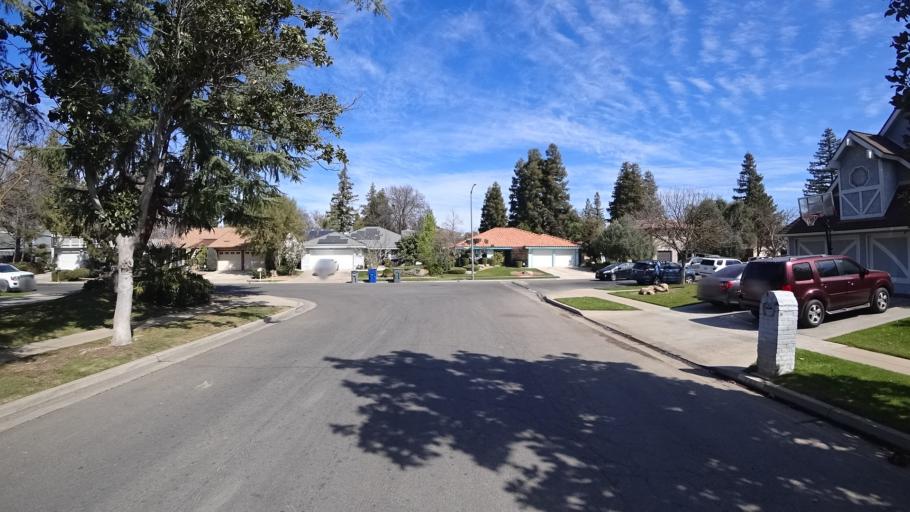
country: US
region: California
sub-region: Fresno County
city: Clovis
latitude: 36.8572
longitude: -119.7784
